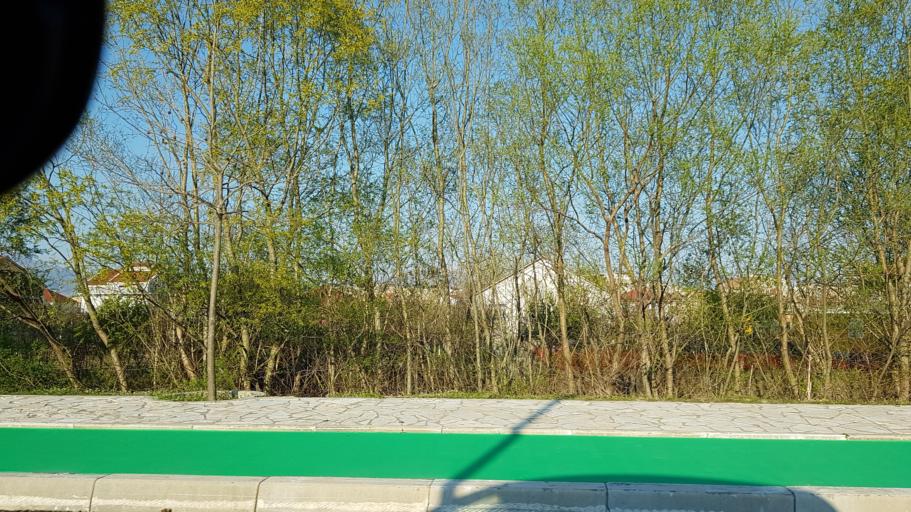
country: AL
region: Shkoder
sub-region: Rrethi i Shkodres
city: Shkoder
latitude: 42.0584
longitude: 19.4982
